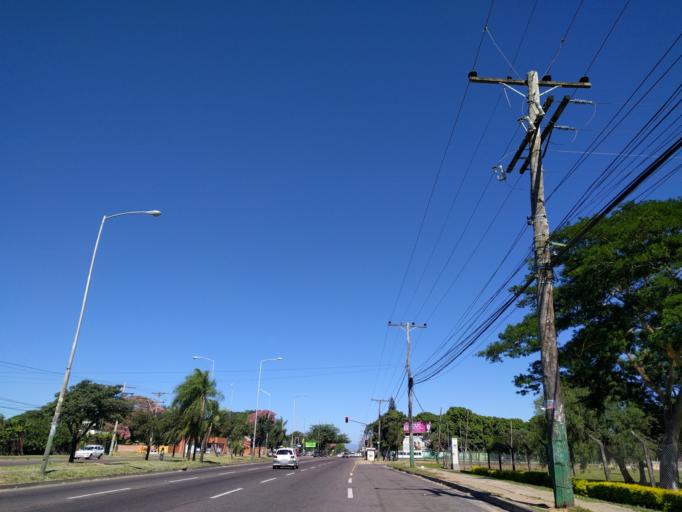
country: BO
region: Santa Cruz
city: Santa Cruz de la Sierra
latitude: -17.8216
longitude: -63.2194
